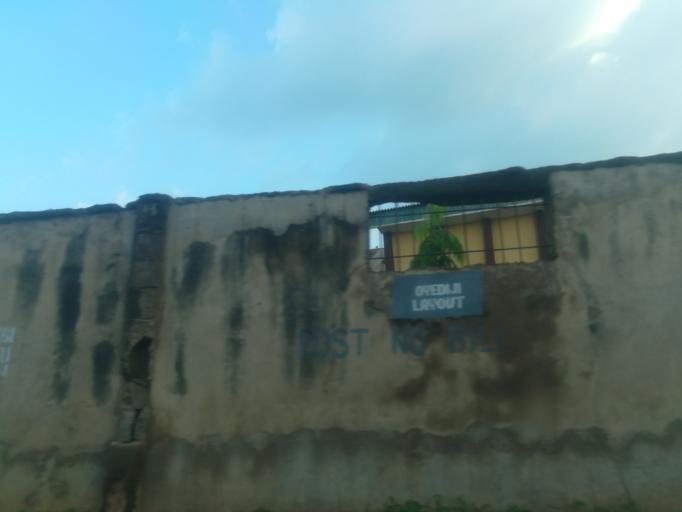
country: NG
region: Oyo
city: Ibadan
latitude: 7.4086
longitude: 3.9495
